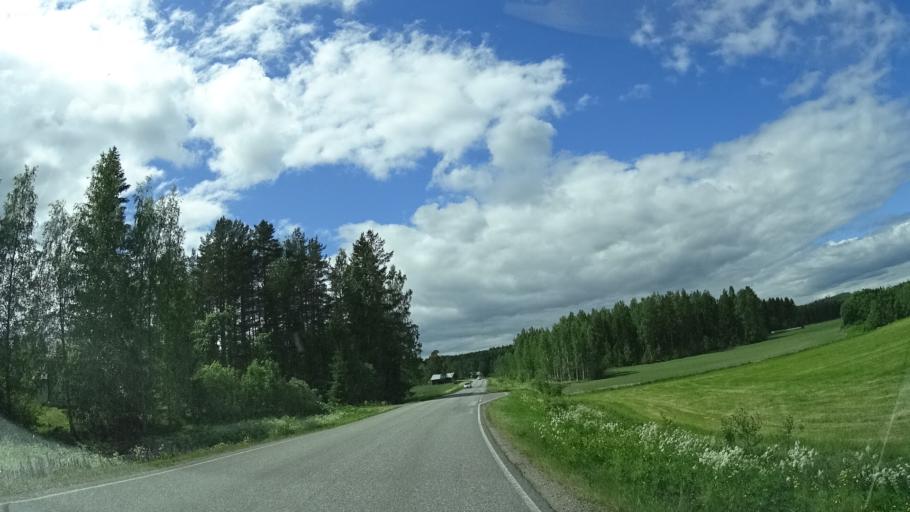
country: FI
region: Central Finland
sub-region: Joutsa
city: Luhanka
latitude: 61.8376
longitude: 25.7535
